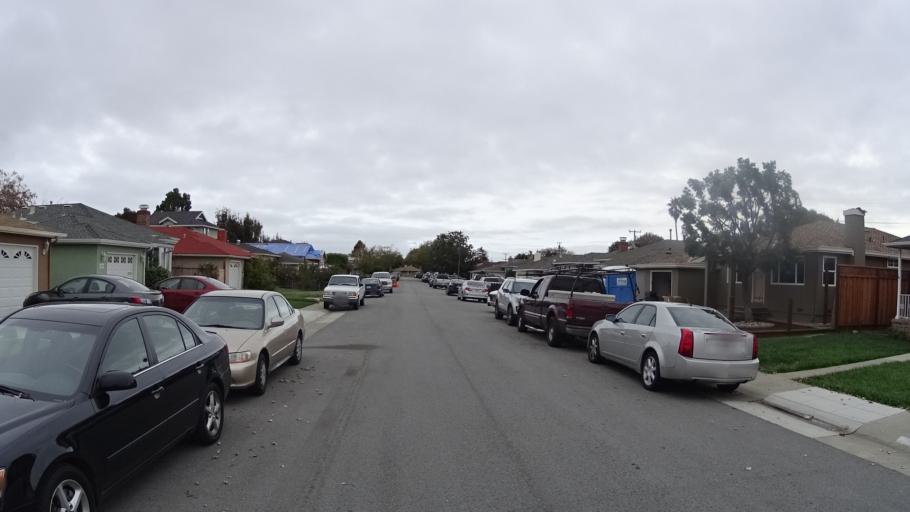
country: US
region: California
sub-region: San Mateo County
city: Belmont
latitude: 37.5367
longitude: -122.2881
